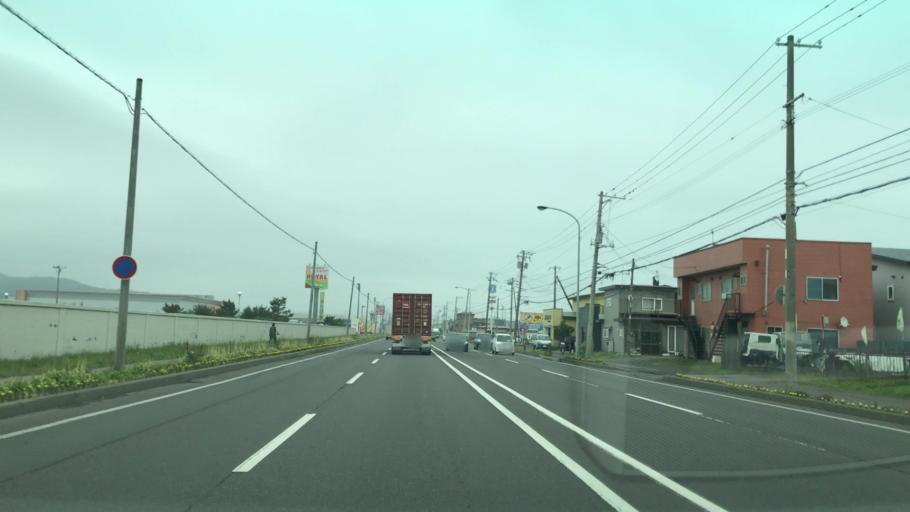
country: JP
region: Hokkaido
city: Muroran
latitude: 42.3693
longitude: 141.0623
